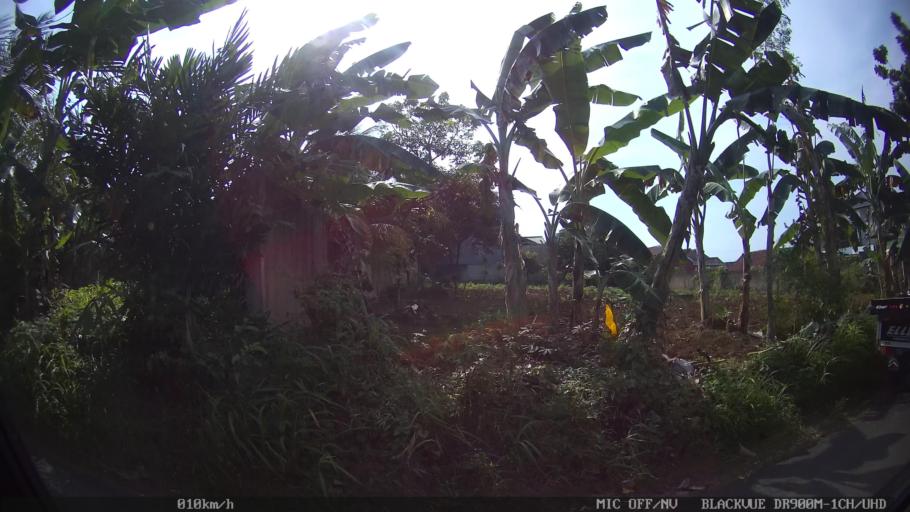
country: ID
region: Lampung
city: Kedaton
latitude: -5.3856
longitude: 105.2243
